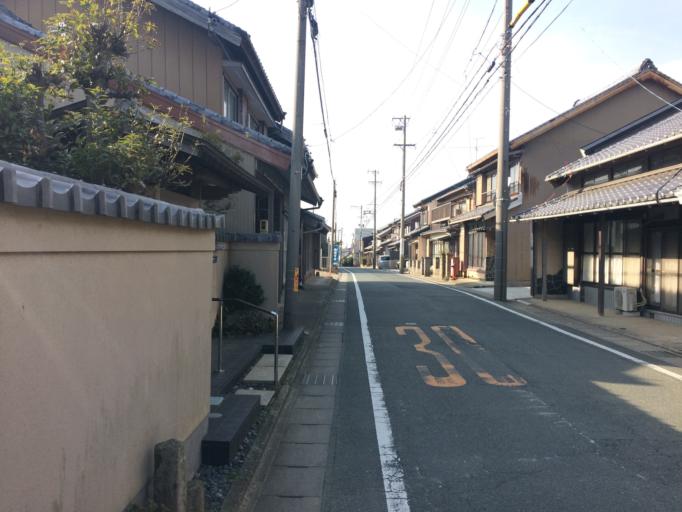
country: JP
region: Shizuoka
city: Kosai-shi
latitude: 34.6858
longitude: 137.5055
